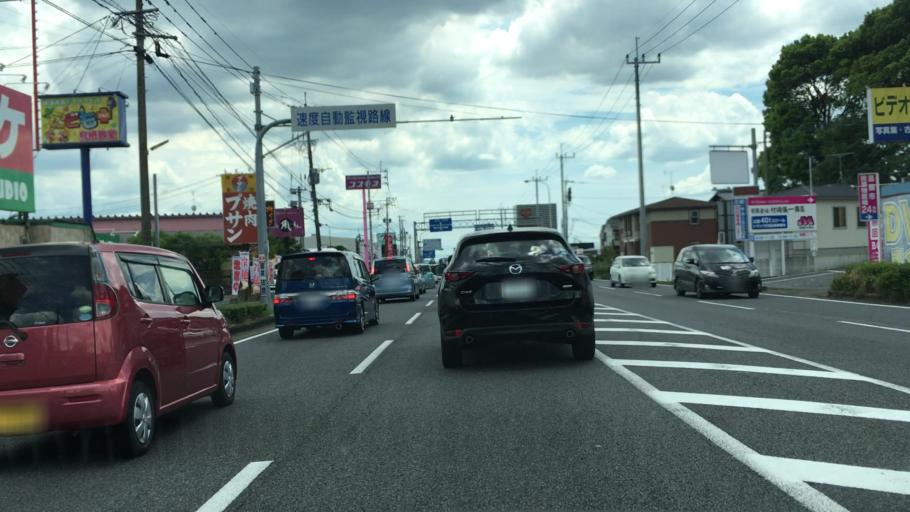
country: JP
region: Saga Prefecture
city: Tosu
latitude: 33.3826
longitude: 130.4992
